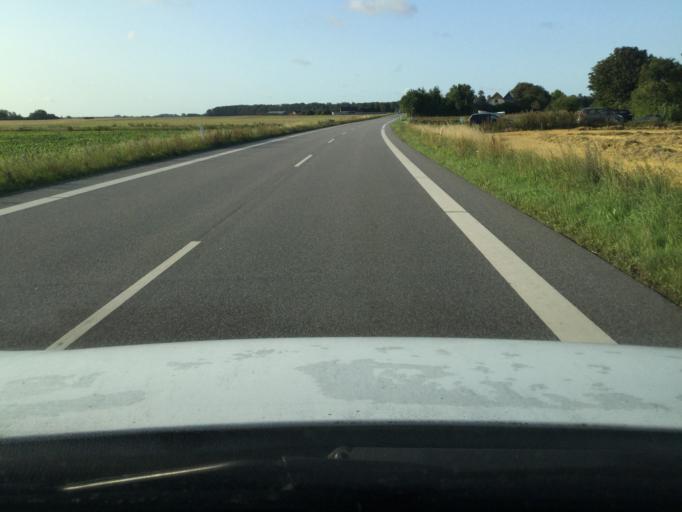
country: DK
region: Zealand
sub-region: Lolland Kommune
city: Rodby
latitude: 54.7425
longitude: 11.3886
